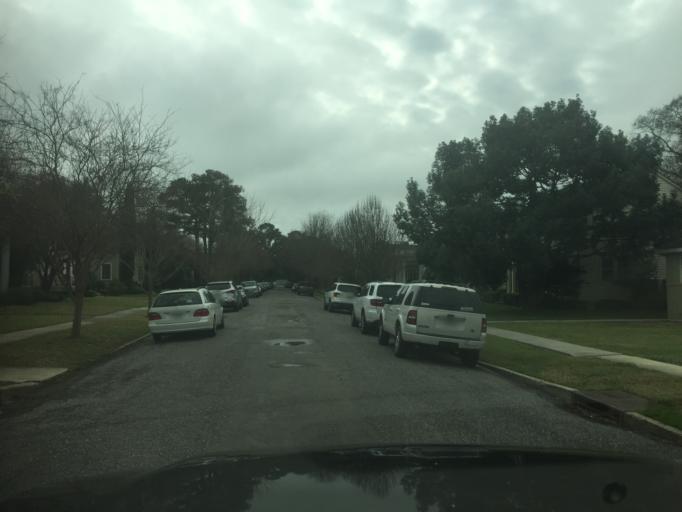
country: US
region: Louisiana
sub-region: Jefferson Parish
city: Metairie
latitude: 29.9988
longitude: -90.1075
